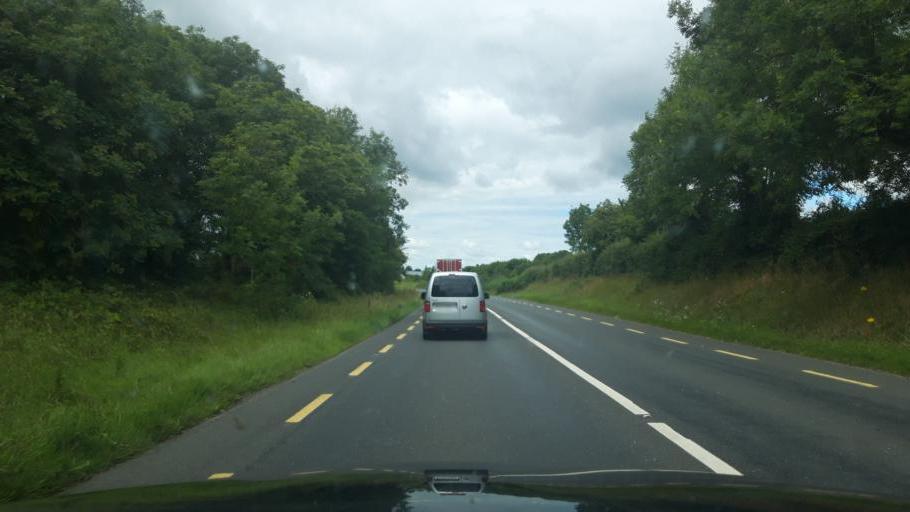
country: IE
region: Munster
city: Carrick-on-Suir
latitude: 52.3929
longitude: -7.5122
